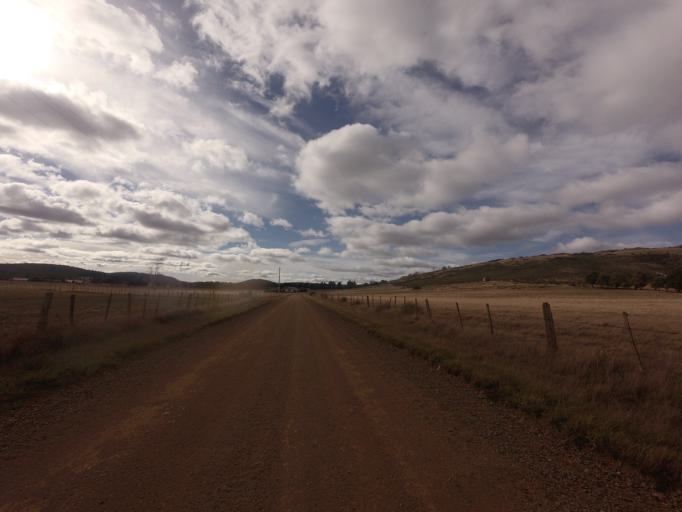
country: AU
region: Tasmania
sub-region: Brighton
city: Bridgewater
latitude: -42.4195
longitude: 147.3929
